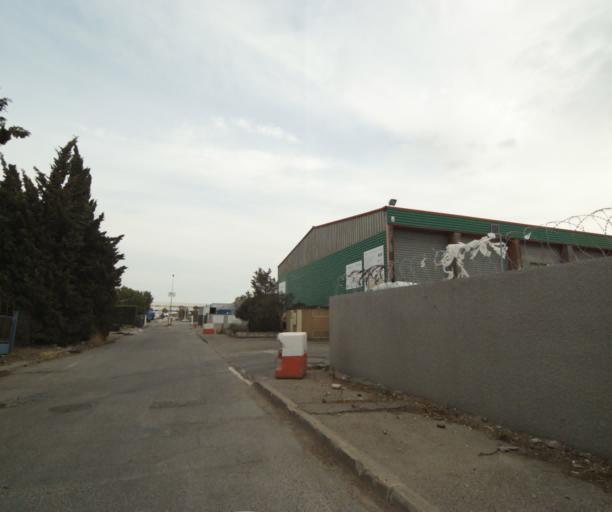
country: FR
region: Provence-Alpes-Cote d'Azur
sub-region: Departement des Bouches-du-Rhone
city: Marignane
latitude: 43.4052
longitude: 5.2002
